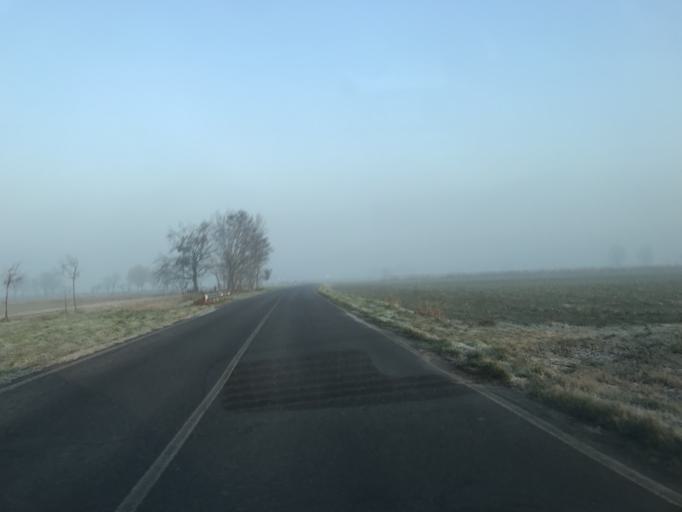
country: IT
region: Lombardy
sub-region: Provincia di Lodi
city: Bargano
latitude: 45.2473
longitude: 9.4388
